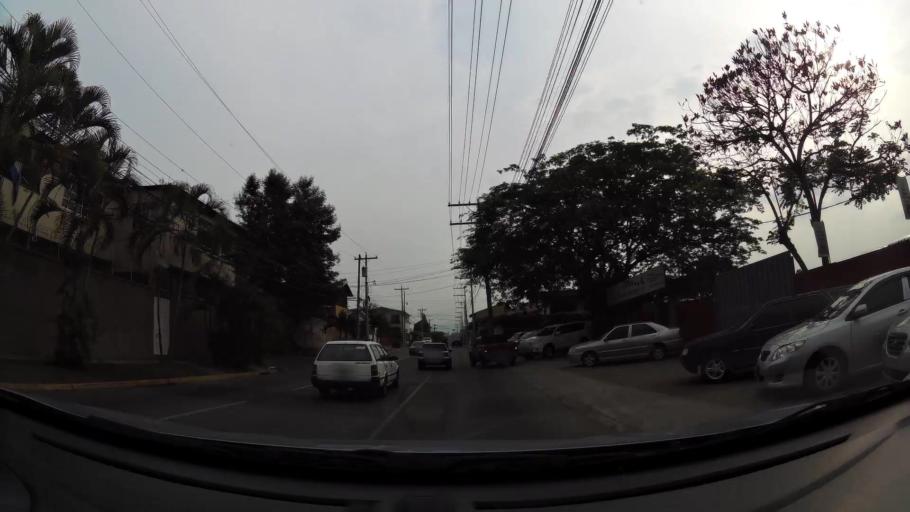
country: HN
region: Francisco Morazan
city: Tegucigalpa
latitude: 14.0841
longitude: -87.1995
